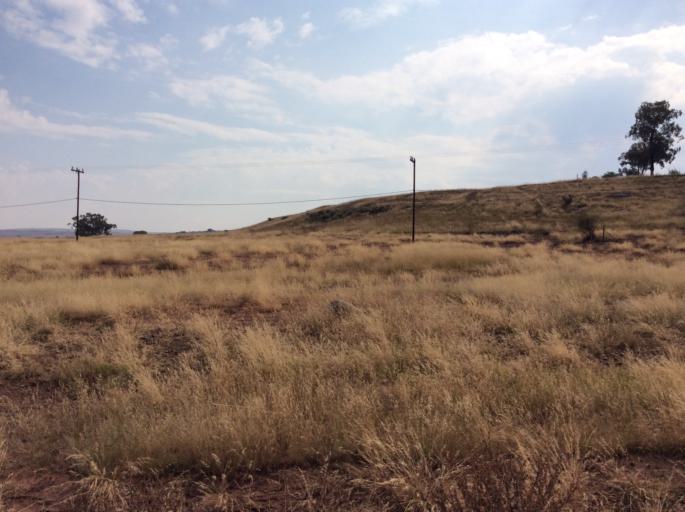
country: LS
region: Mafeteng
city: Mafeteng
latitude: -29.9886
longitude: 27.0057
